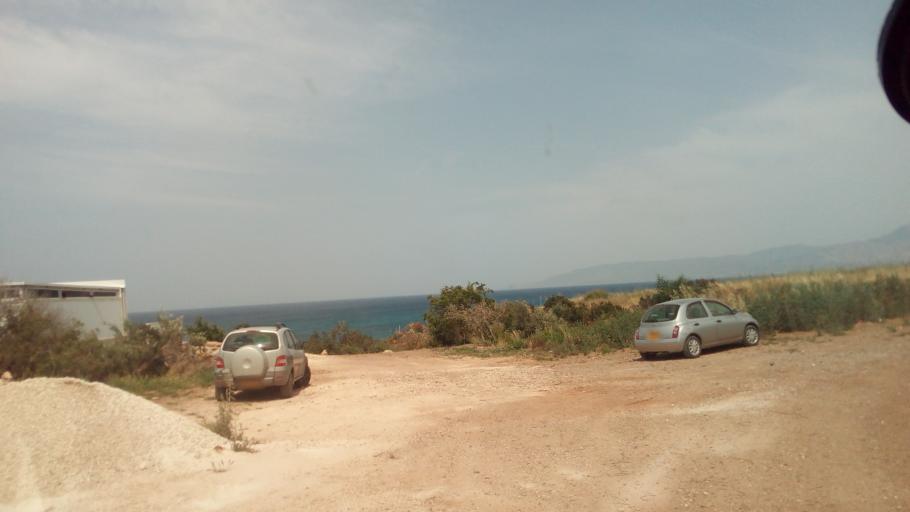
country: CY
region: Pafos
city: Polis
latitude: 35.0460
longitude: 32.3600
